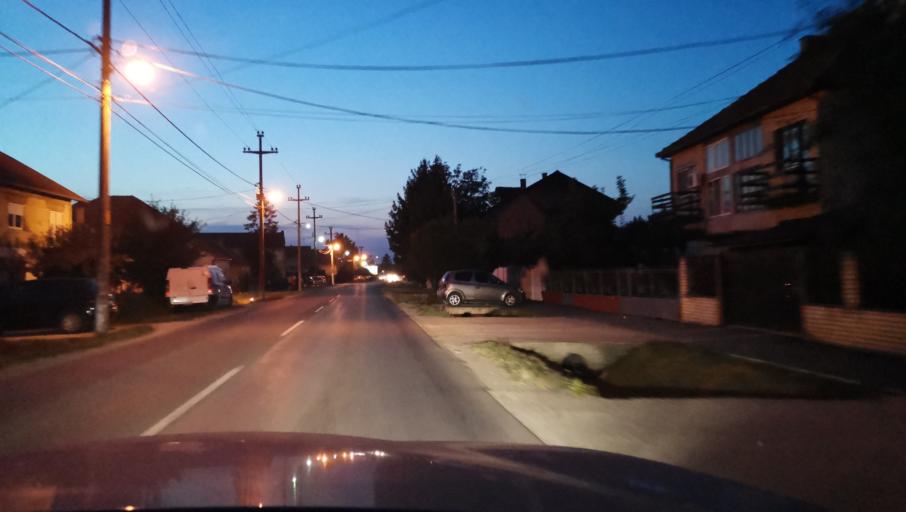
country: RS
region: Central Serbia
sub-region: Belgrade
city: Surcin
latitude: 44.7575
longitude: 20.2569
